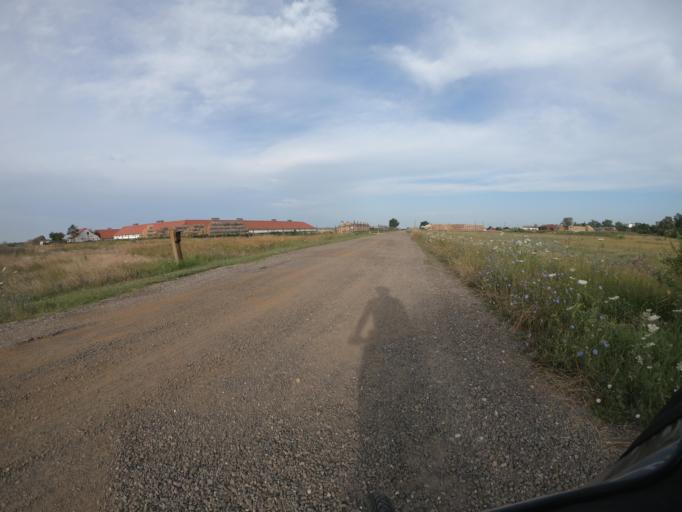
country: HU
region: Hajdu-Bihar
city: Hortobagy
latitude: 47.6022
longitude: 21.0758
